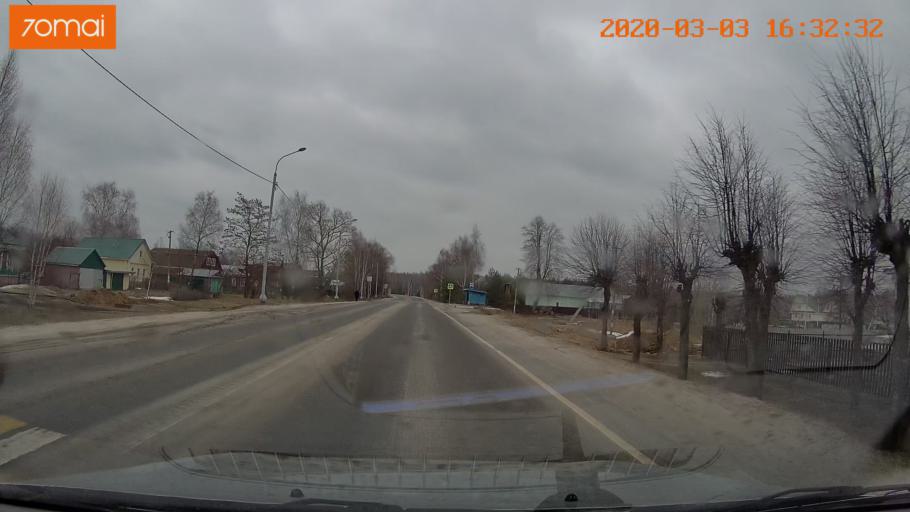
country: RU
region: Moskovskaya
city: Konobeyevo
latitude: 55.4200
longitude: 38.7335
